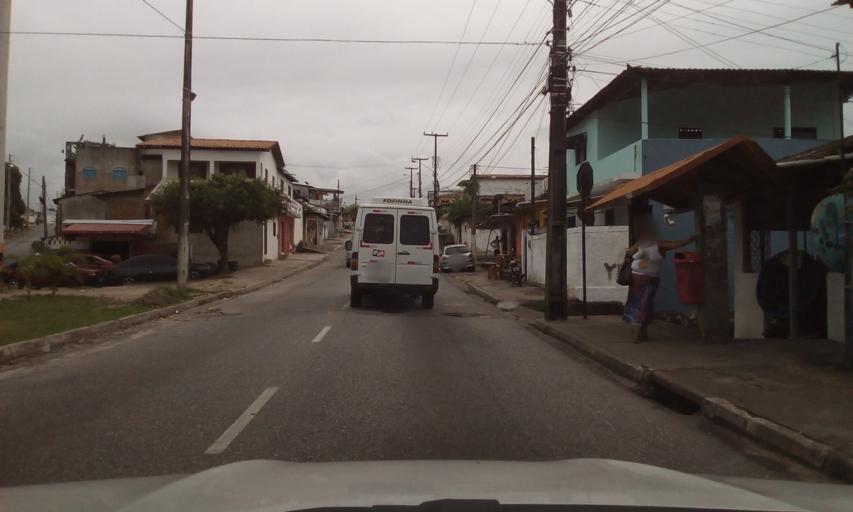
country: BR
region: Paraiba
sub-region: Joao Pessoa
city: Joao Pessoa
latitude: -7.1051
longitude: -34.8659
